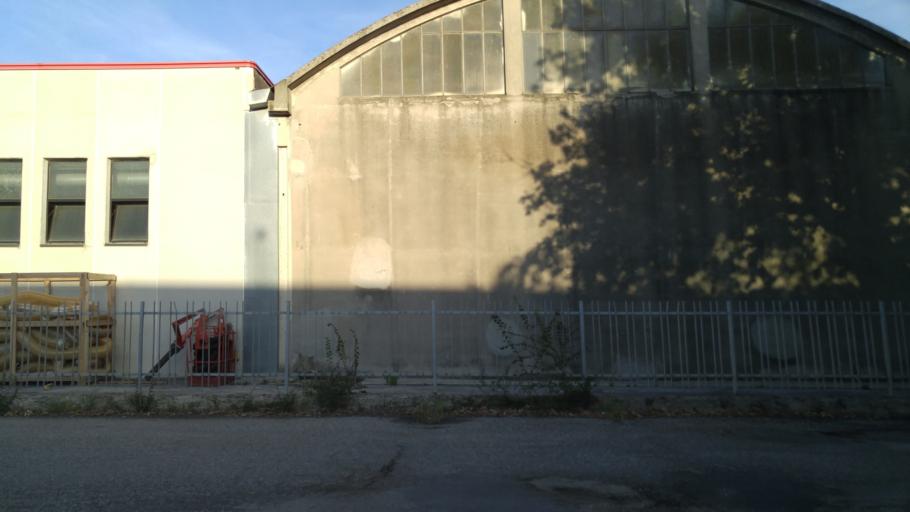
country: IT
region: The Marches
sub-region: Provincia di Pesaro e Urbino
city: Lucrezia
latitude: 43.7638
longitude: 12.9359
